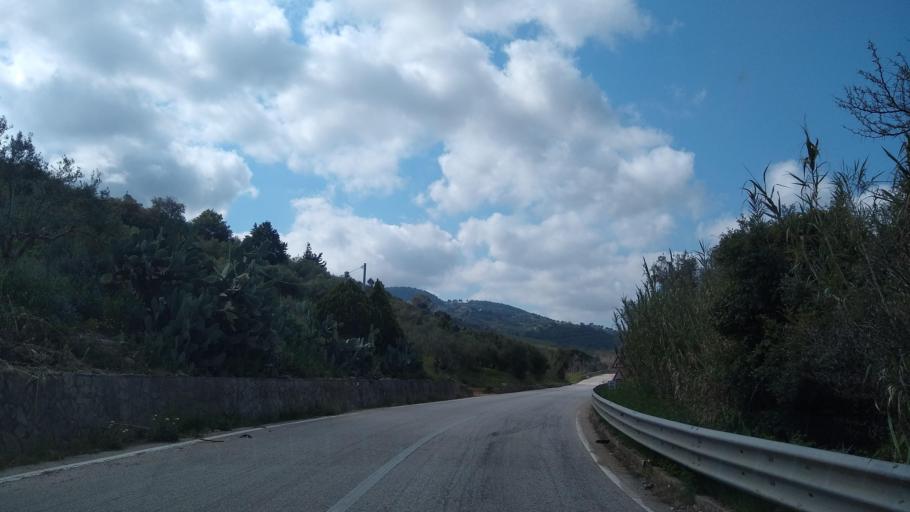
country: IT
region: Sicily
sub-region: Trapani
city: Calatafimi
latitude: 37.9517
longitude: 12.8625
